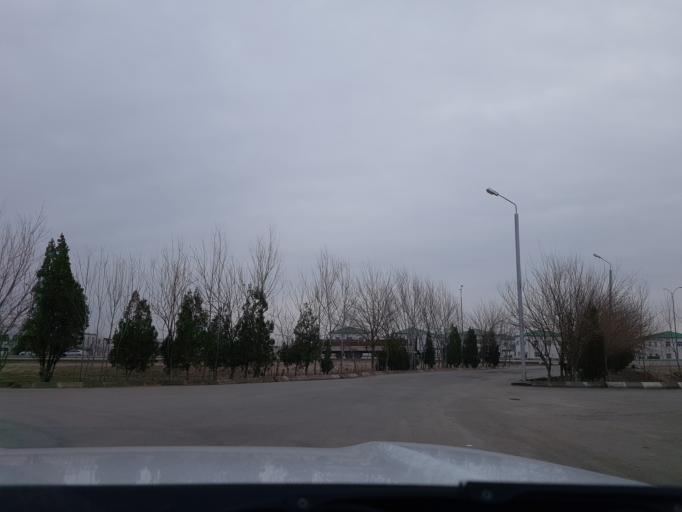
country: TM
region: Ahal
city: Tejen
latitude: 37.3723
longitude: 60.5194
